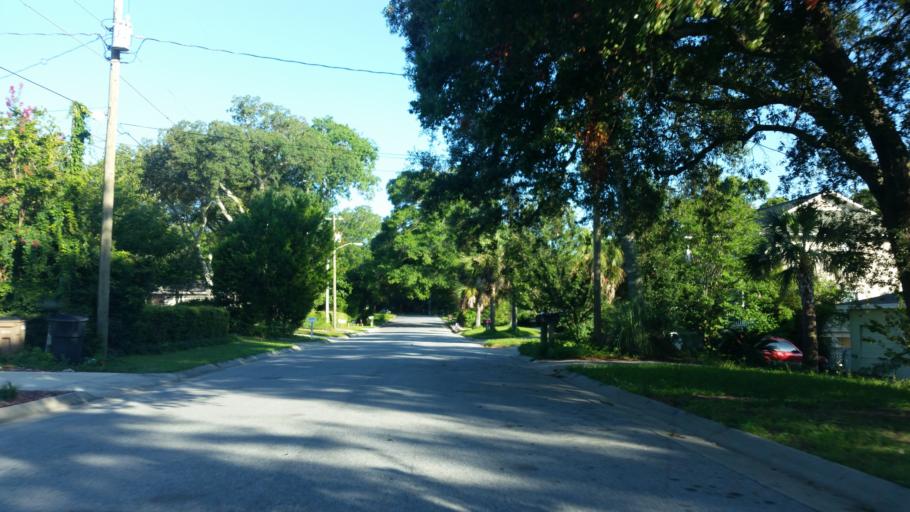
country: US
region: Florida
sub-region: Escambia County
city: Ferry Pass
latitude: 30.4949
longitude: -87.1607
